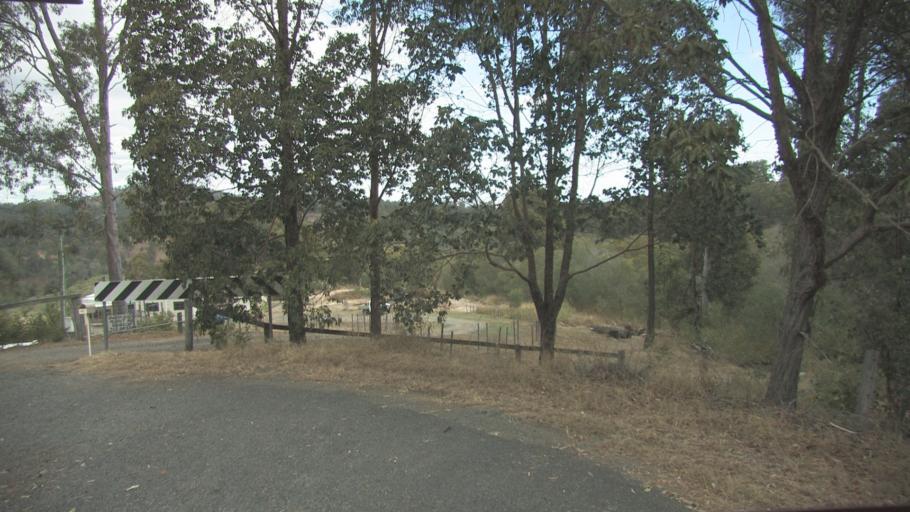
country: AU
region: Queensland
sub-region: Logan
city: Cedar Vale
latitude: -27.9027
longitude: 153.0387
